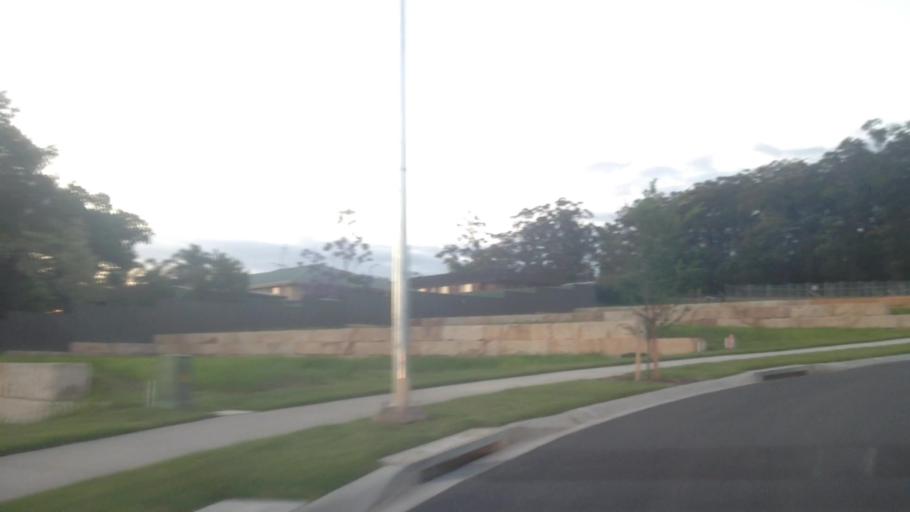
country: AU
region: New South Wales
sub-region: Lake Macquarie Shire
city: Cooranbong
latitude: -33.0709
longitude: 151.4569
